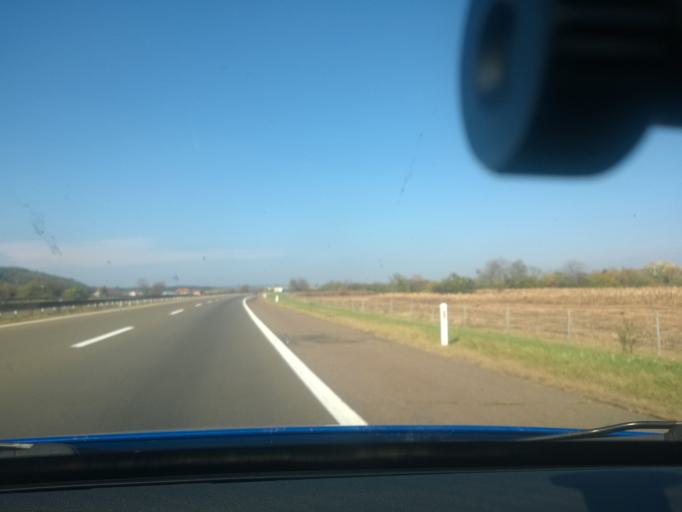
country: RS
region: Central Serbia
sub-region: Sumadijski Okrug
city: Batocina
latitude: 44.1205
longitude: 21.1438
